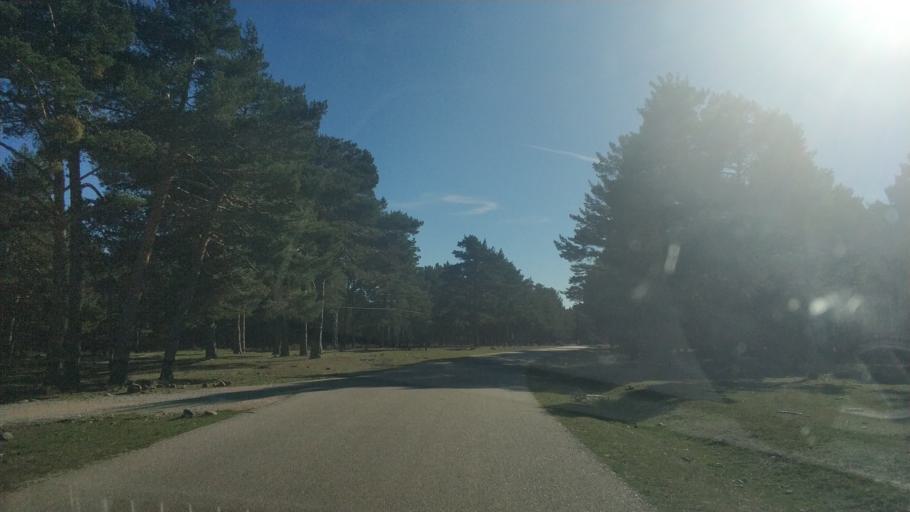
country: ES
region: Castille and Leon
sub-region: Provincia de Soria
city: Vinuesa
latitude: 41.9556
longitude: -2.7825
